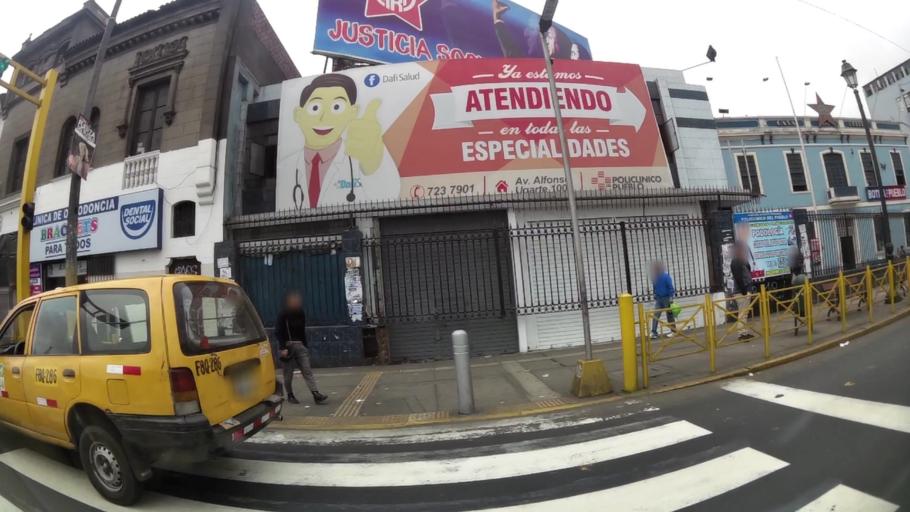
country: PE
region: Lima
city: Lima
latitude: -12.0528
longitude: -77.0424
